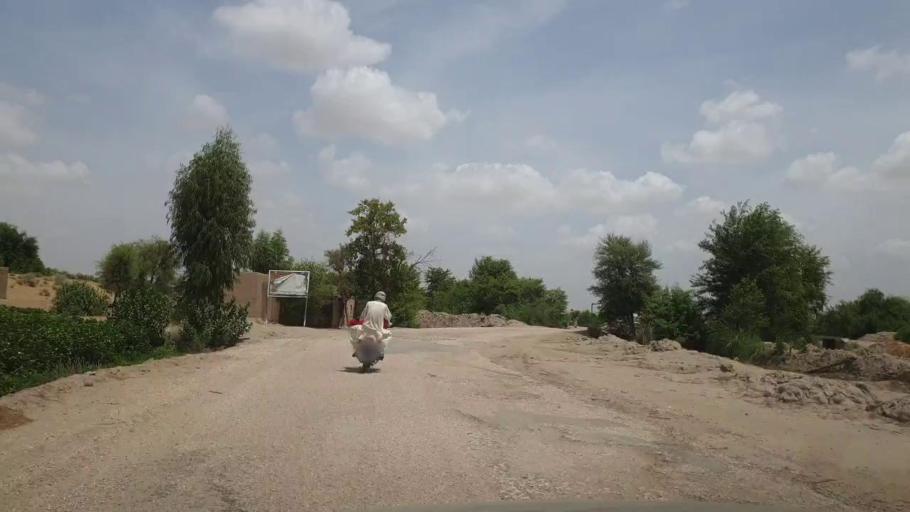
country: PK
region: Sindh
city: Kot Diji
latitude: 27.2165
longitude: 69.1093
